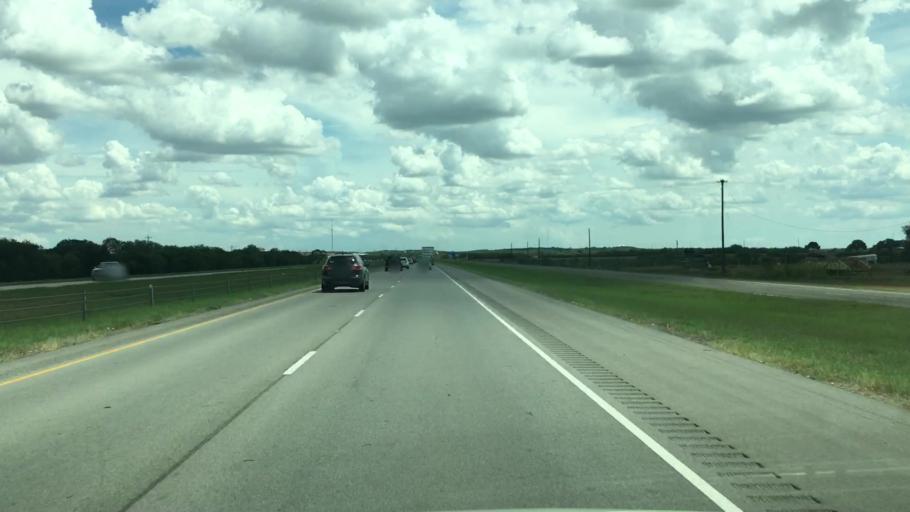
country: US
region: Texas
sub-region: Live Oak County
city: George West
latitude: 28.2717
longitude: -97.9450
